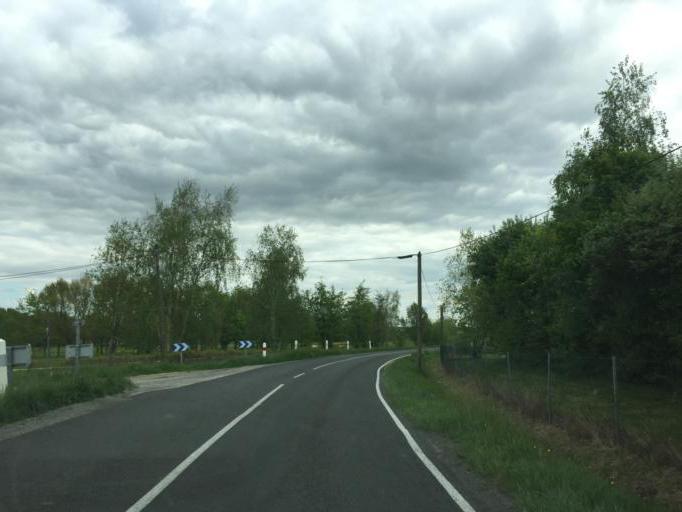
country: FR
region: Rhone-Alpes
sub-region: Departement de l'Ain
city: Amberieux-en-Dombes
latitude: 45.9692
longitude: 4.9370
